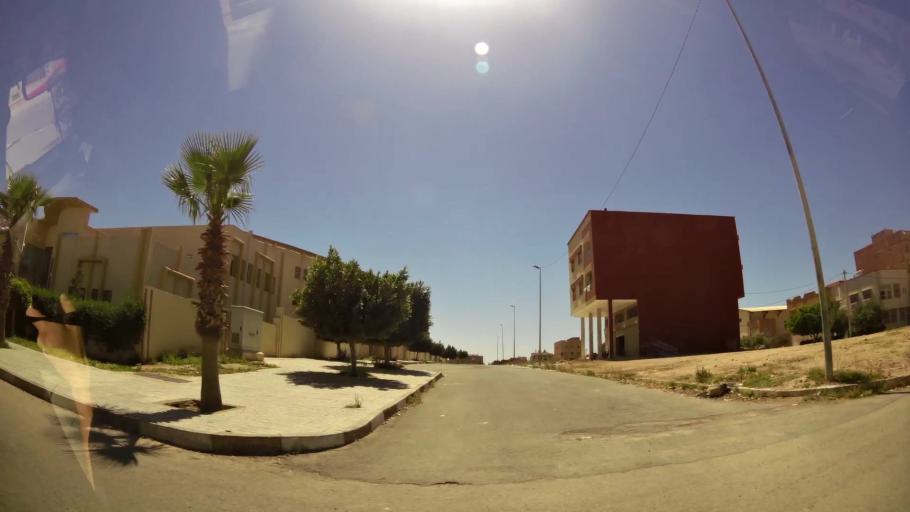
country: MA
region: Oriental
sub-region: Oujda-Angad
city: Oujda
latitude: 34.6618
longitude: -1.8737
